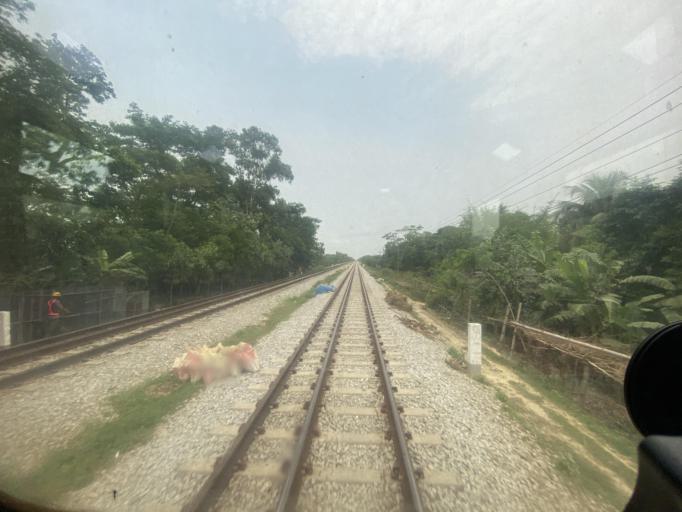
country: BD
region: Chittagong
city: Laksham
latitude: 23.3221
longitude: 91.1426
